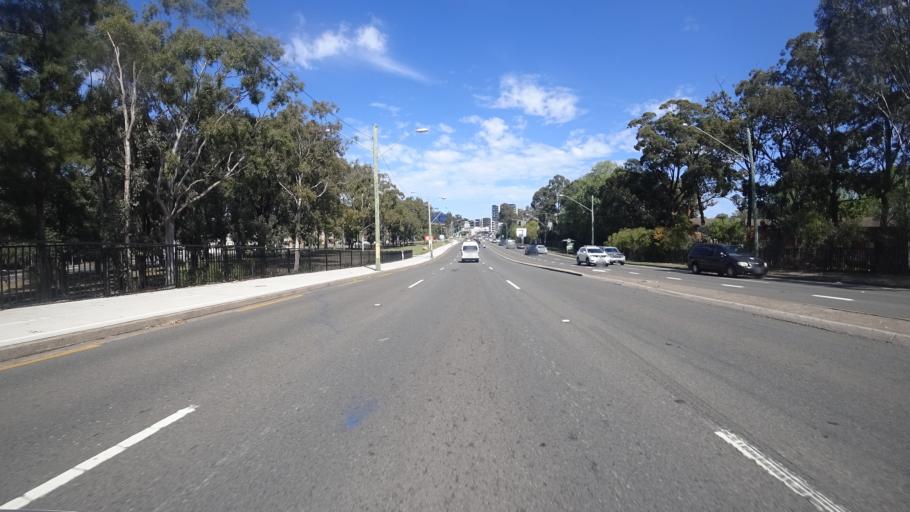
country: AU
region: New South Wales
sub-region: Fairfield
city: Liverpool
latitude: -33.9128
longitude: 150.9345
